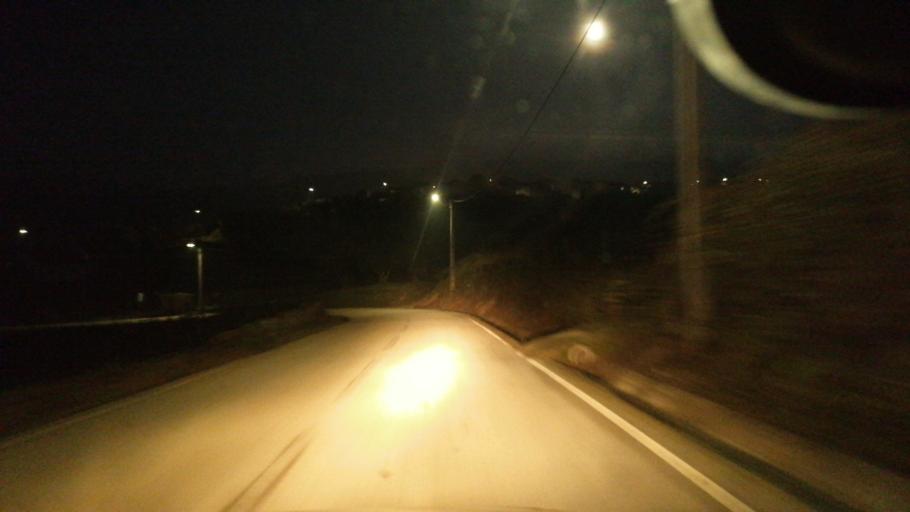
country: PT
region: Vila Real
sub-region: Sabrosa
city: Sabrosa
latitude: 41.3075
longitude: -7.5165
